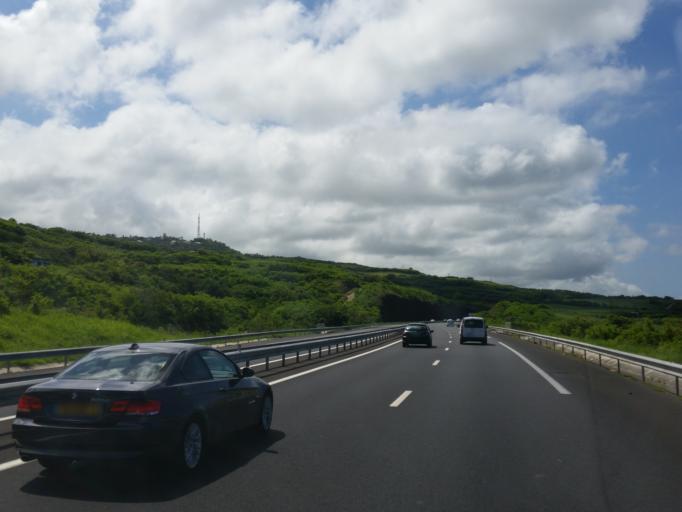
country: RE
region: Reunion
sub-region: Reunion
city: Trois-Bassins
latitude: -21.0780
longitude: 55.2530
